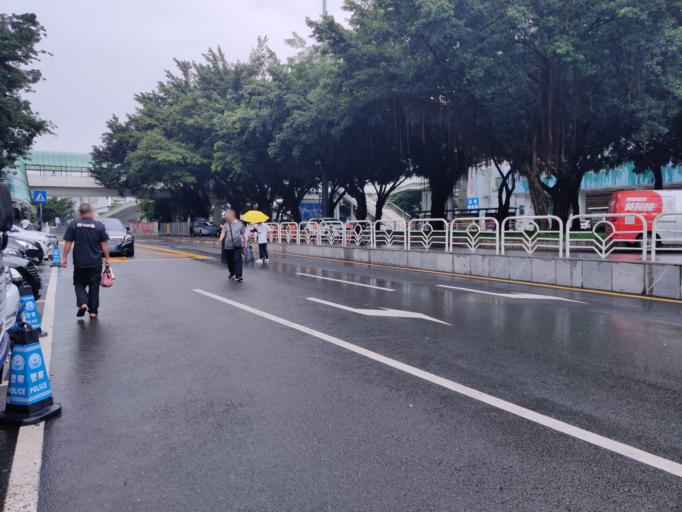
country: CN
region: Guangdong
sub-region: Shenzhen
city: Shenzhen
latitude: 22.5307
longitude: 114.1115
